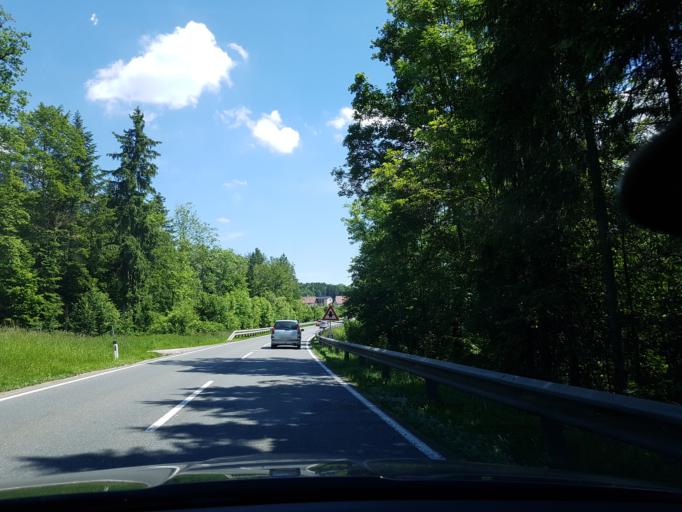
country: AT
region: Salzburg
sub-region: Politischer Bezirk Salzburg-Umgebung
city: Elixhausen
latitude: 47.8505
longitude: 13.0505
